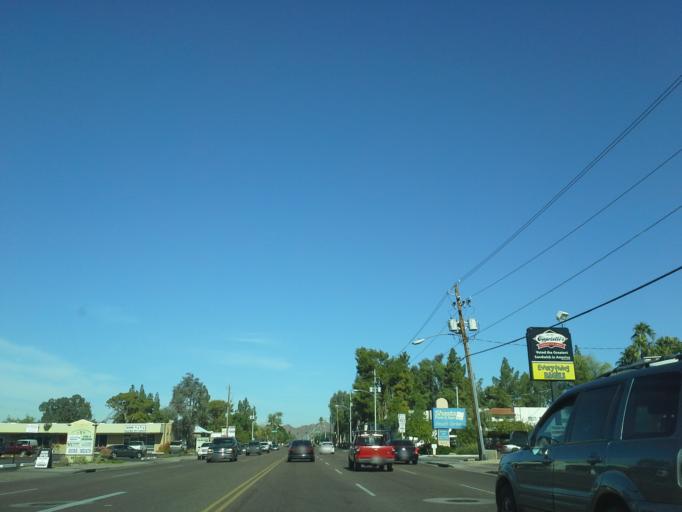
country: US
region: Arizona
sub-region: Maricopa County
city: Phoenix
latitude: 33.5244
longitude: -112.0475
